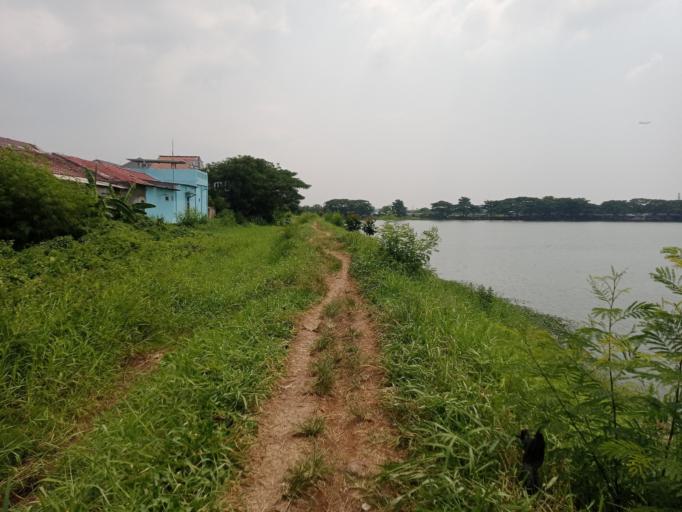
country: ID
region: Banten
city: Tangerang
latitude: -6.1644
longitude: 106.5910
